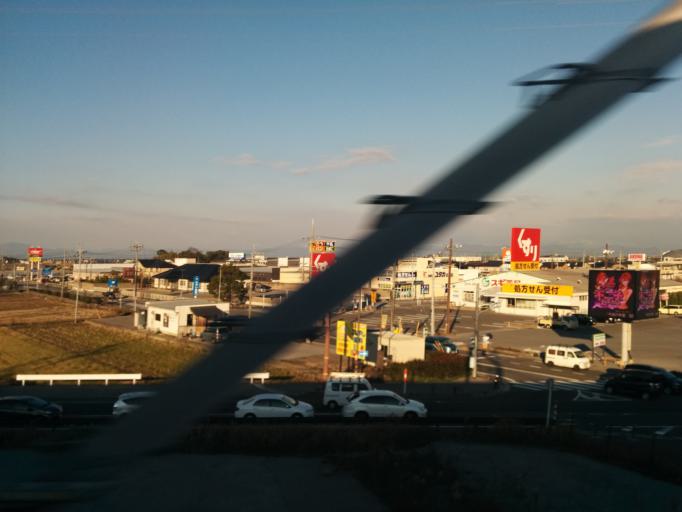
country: JP
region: Shiga Prefecture
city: Nagahama
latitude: 35.3358
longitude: 136.2958
